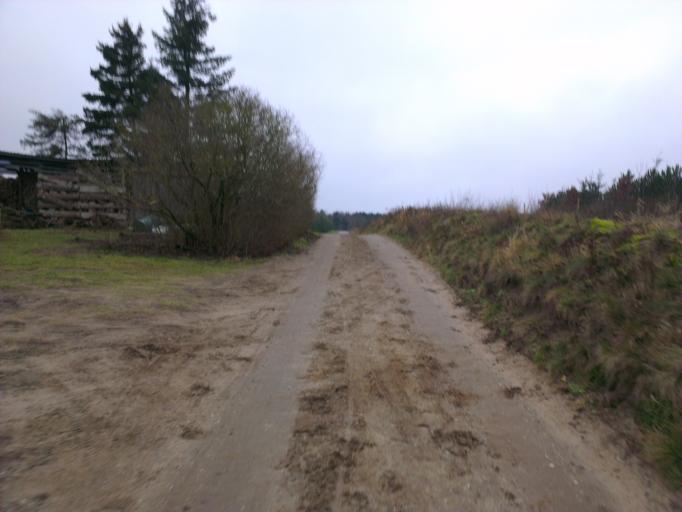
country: DK
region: Capital Region
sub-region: Frederikssund Kommune
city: Jaegerspris
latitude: 55.8448
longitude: 12.0036
